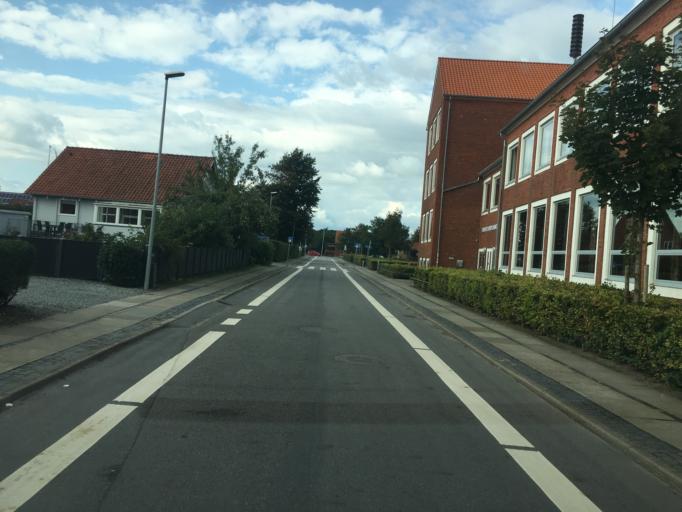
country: DK
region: South Denmark
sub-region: Tonder Kommune
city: Tonder
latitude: 54.9367
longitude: 8.8581
